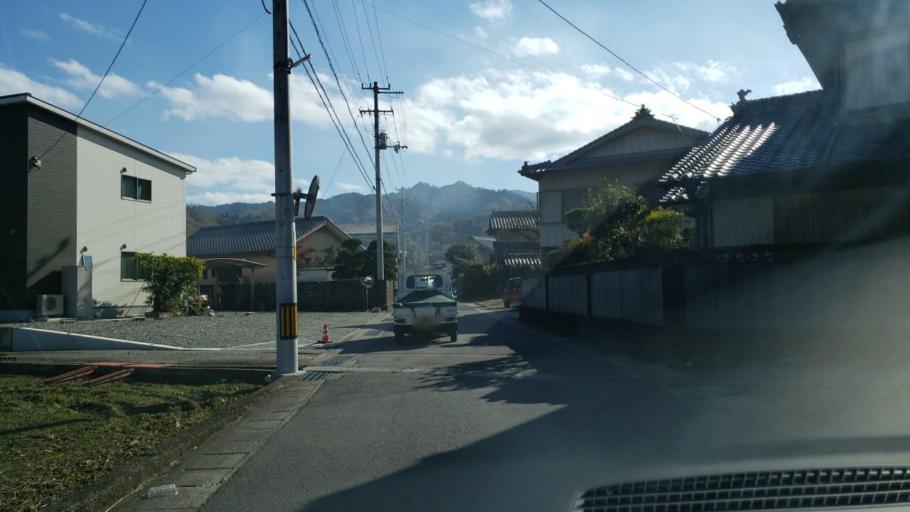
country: JP
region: Tokushima
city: Wakimachi
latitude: 34.0291
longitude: 134.0297
